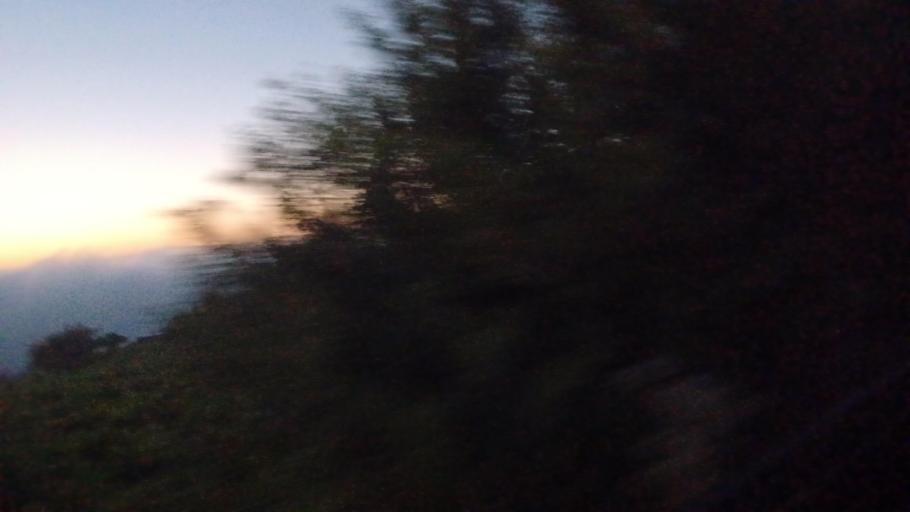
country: CY
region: Pafos
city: Tala
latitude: 34.8600
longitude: 32.4720
